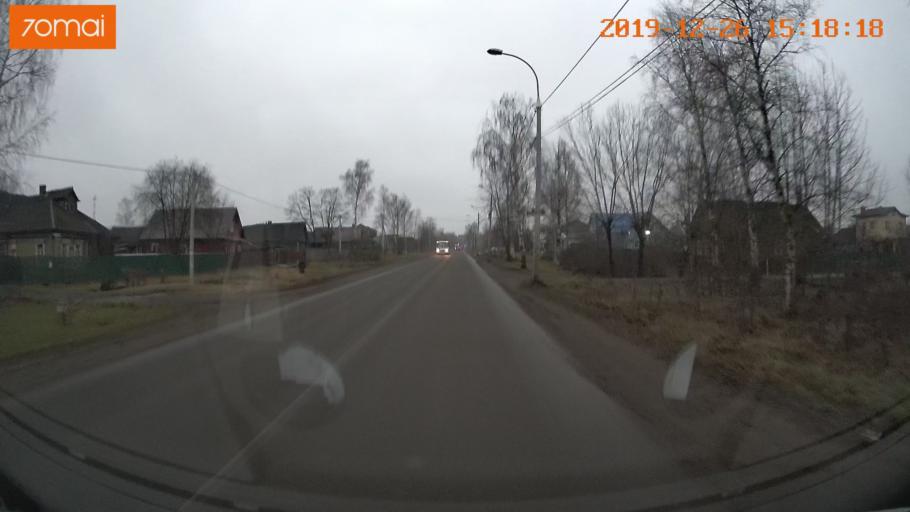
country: RU
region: Jaroslavl
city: Rybinsk
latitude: 58.0705
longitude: 38.8439
